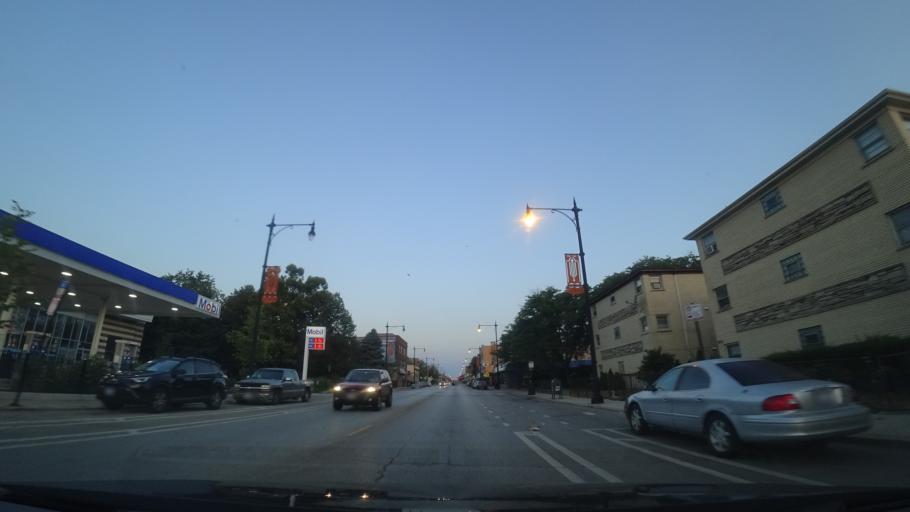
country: US
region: Illinois
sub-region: Cook County
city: Lincolnwood
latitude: 41.9682
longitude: -87.7348
